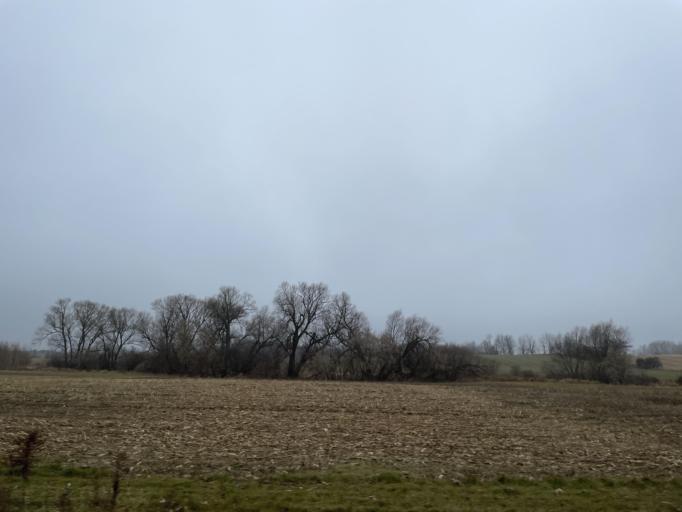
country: CA
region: Ontario
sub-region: Wellington County
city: Guelph
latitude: 43.4888
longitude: -80.3412
